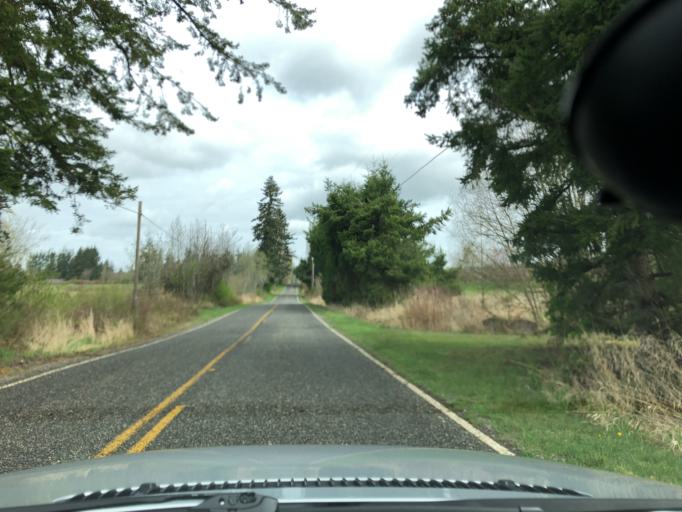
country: US
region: Washington
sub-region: Whatcom County
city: Blaine
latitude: 48.9743
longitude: -122.7039
